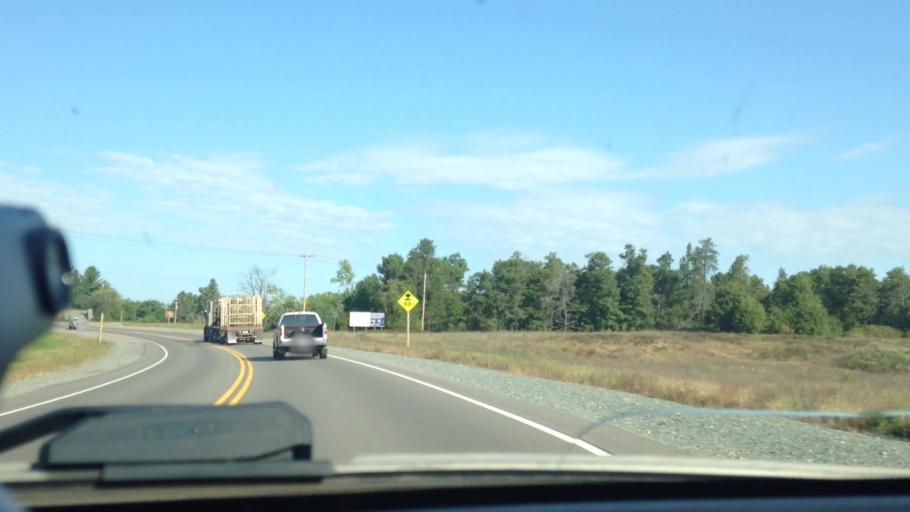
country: US
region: Michigan
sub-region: Dickinson County
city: Iron Mountain
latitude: 45.8740
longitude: -88.0850
